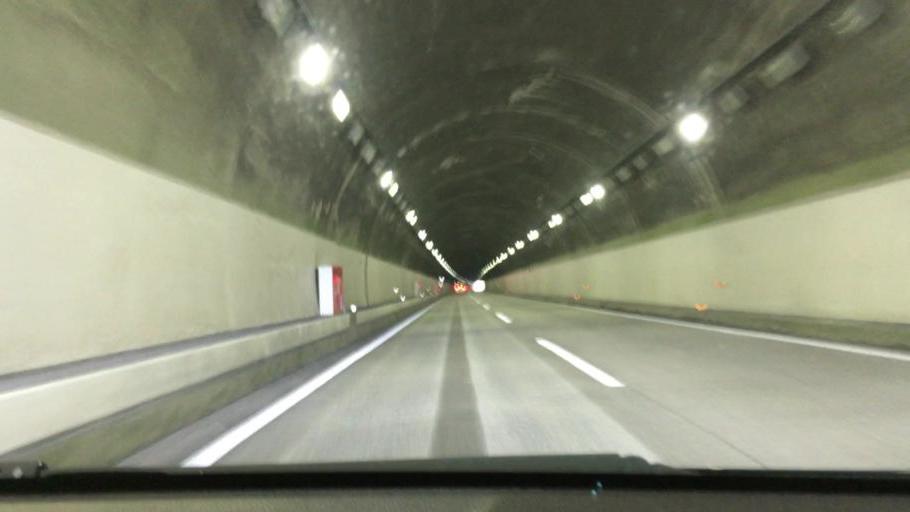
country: JP
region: Yamaguchi
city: Tokuyama
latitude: 34.0795
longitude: 131.7941
